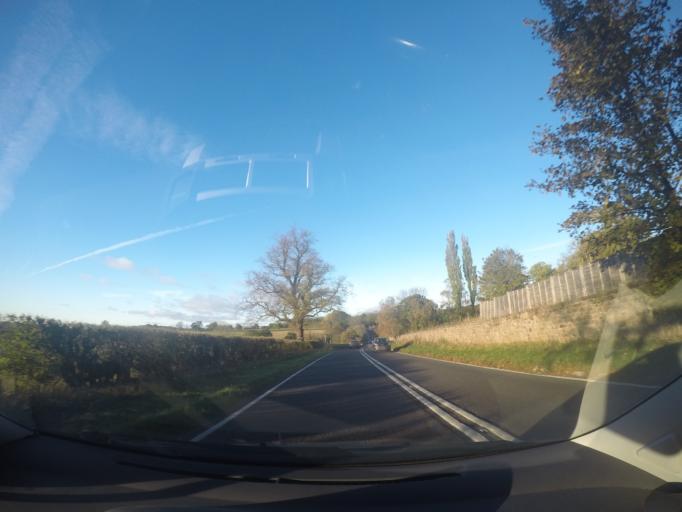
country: GB
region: England
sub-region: City and Borough of Leeds
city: Thorner
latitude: 53.8485
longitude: -1.4028
